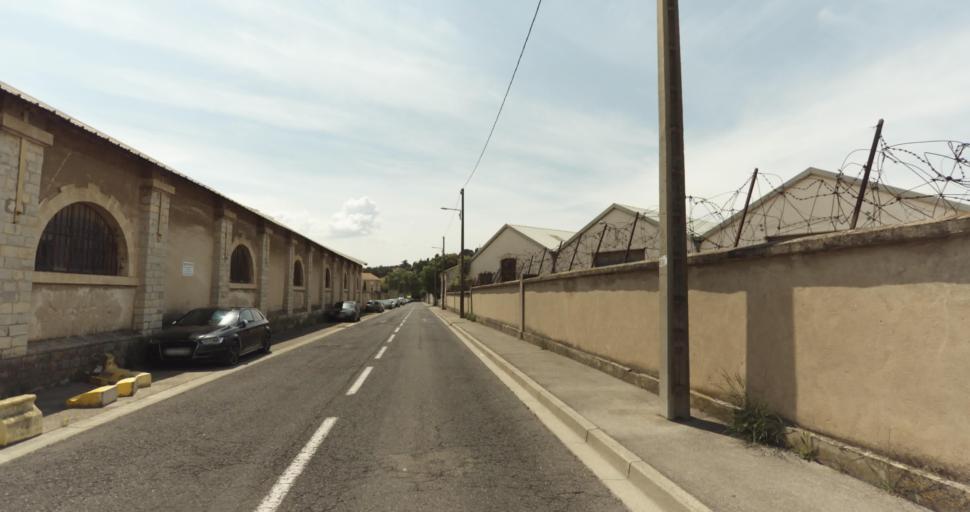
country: FR
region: Languedoc-Roussillon
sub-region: Departement du Gard
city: Nimes
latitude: 43.8489
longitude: 4.3686
